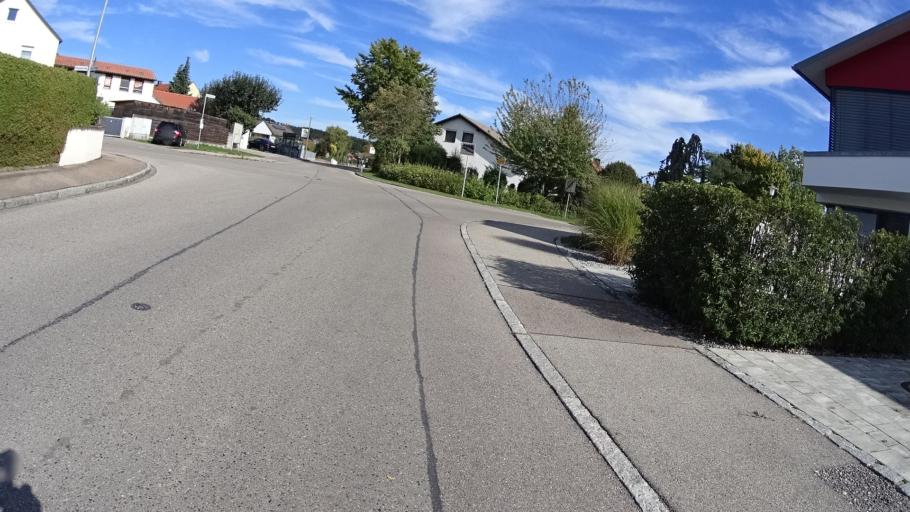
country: DE
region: Bavaria
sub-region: Upper Bavaria
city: Gaimersheim
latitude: 48.8344
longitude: 11.3624
